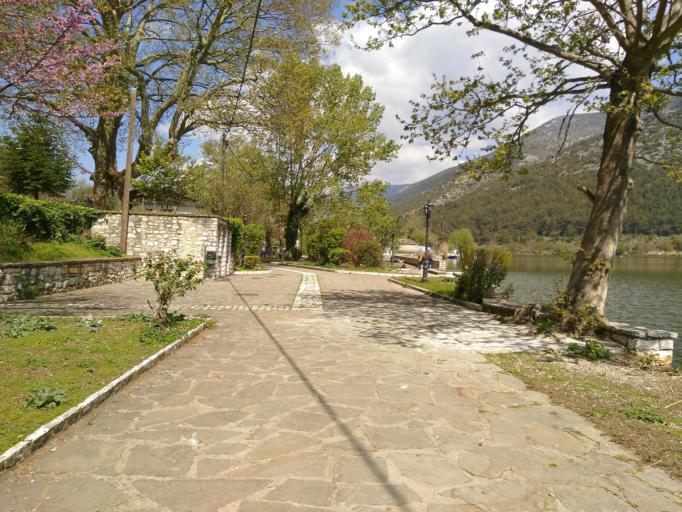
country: GR
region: Epirus
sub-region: Nomos Ioanninon
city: Ioannina
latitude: 39.6790
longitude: 20.8765
